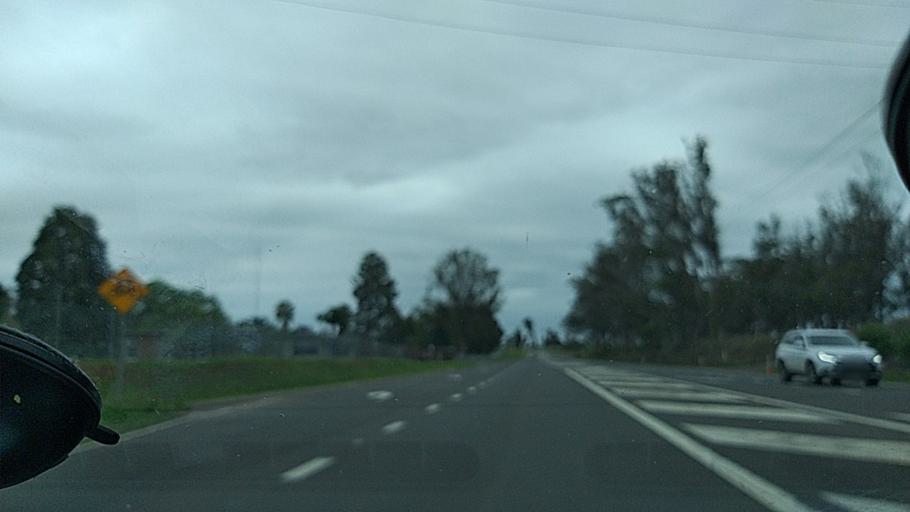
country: AU
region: New South Wales
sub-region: Penrith Municipality
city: Glenmore Park
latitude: -33.8113
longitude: 150.6931
